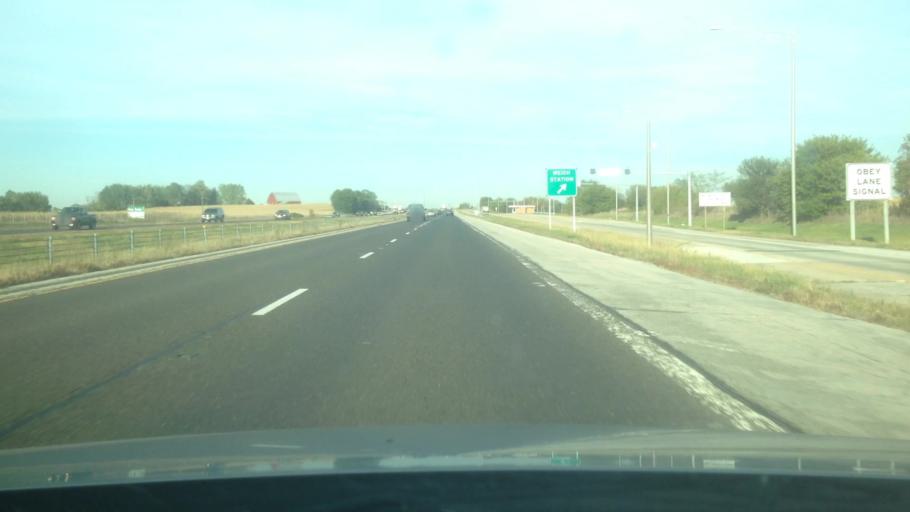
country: US
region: Illinois
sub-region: Will County
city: Peotone
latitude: 41.3586
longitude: -87.8071
